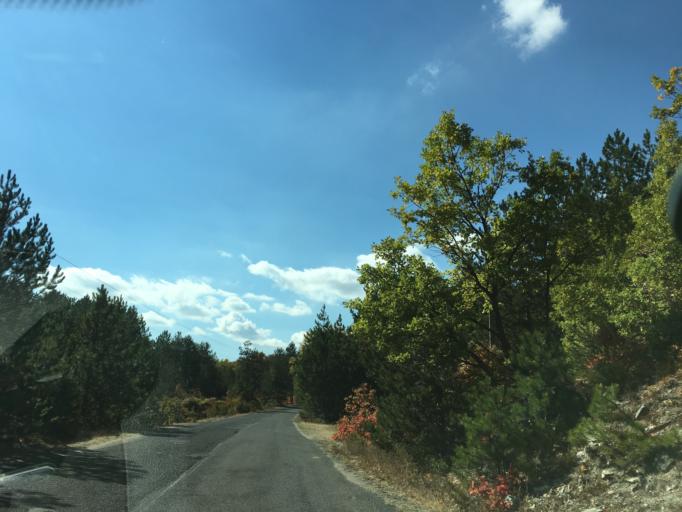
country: BG
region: Kurdzhali
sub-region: Obshtina Krumovgrad
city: Krumovgrad
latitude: 41.5450
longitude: 25.5233
